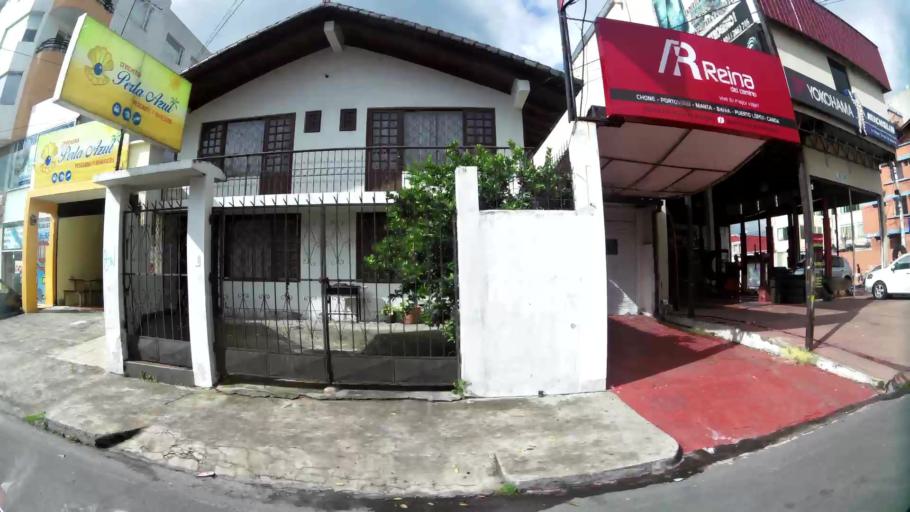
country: EC
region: Pichincha
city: Sangolqui
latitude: -0.3050
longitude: -78.4559
